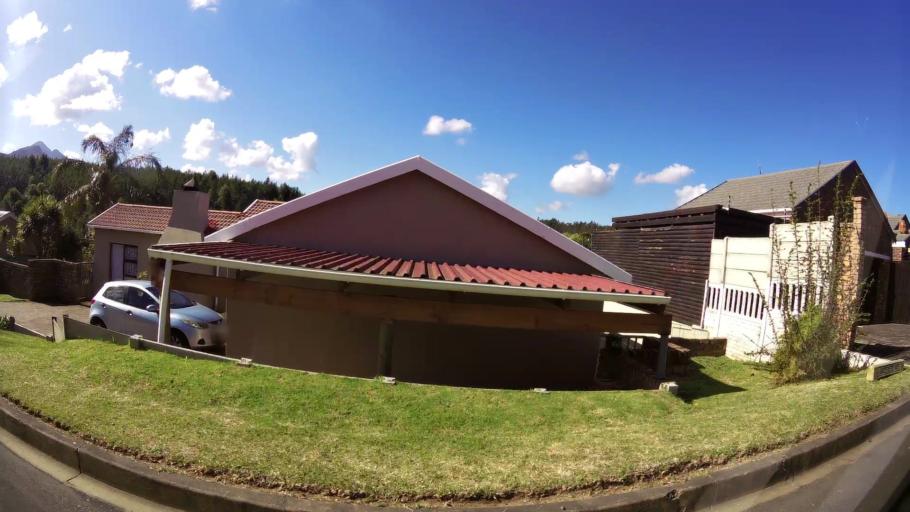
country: ZA
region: Western Cape
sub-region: Eden District Municipality
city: George
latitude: -33.9481
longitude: 22.4809
